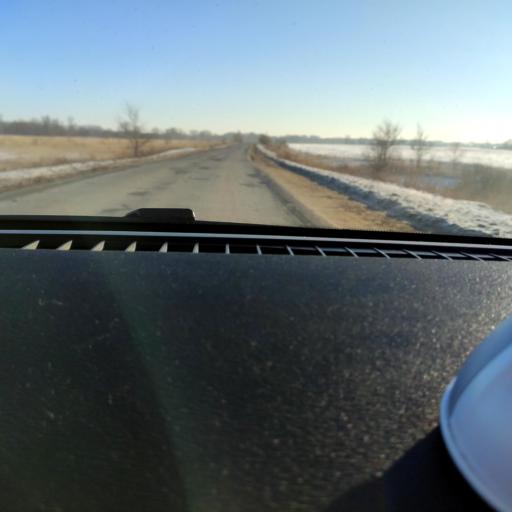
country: RU
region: Samara
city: Spiridonovka
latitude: 53.1250
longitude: 50.6243
